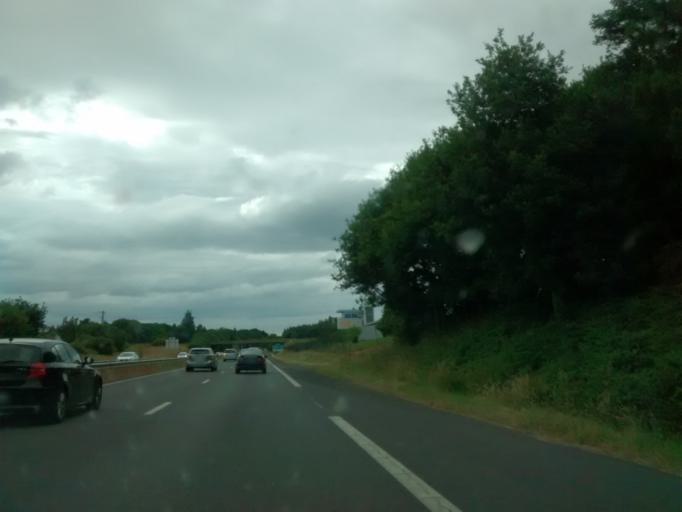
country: FR
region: Brittany
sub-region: Departement des Cotes-d'Armor
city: Plenee-Jugon
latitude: 48.3967
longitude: -2.4031
